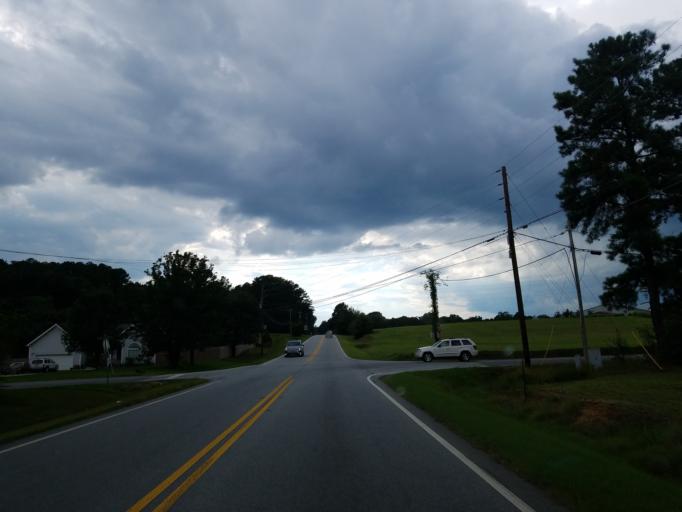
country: US
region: Georgia
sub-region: Floyd County
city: Shannon
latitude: 34.3851
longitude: -85.1634
